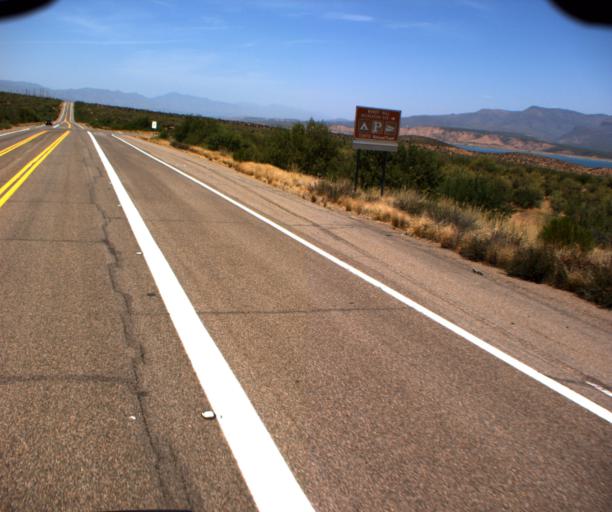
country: US
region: Arizona
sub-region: Gila County
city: Tonto Basin
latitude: 33.6475
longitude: -111.0942
